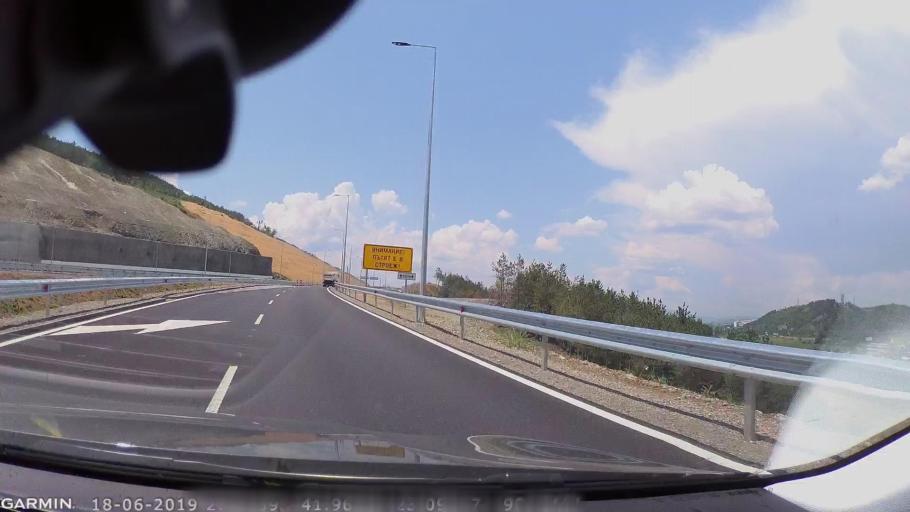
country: BG
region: Blagoevgrad
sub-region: Obshtina Blagoevgrad
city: Blagoevgrad
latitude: 41.9648
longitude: 23.0967
